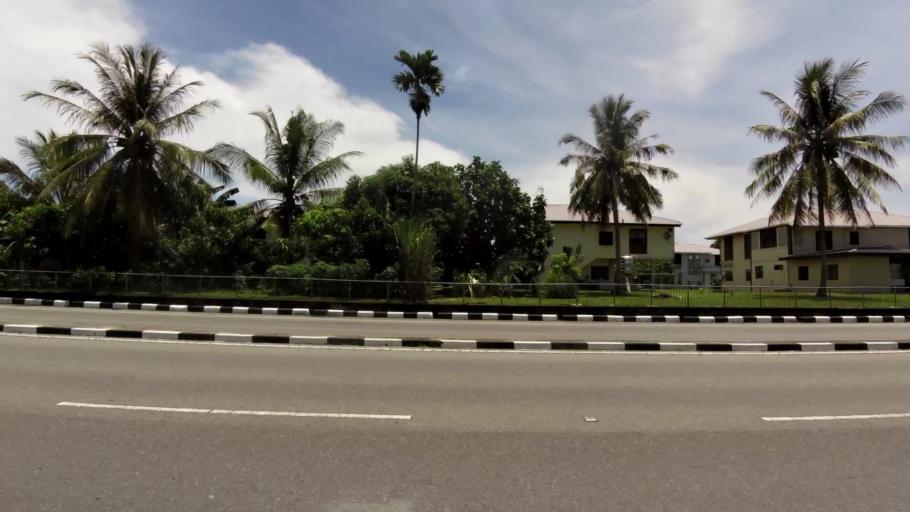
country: BN
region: Belait
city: Kuala Belait
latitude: 4.5825
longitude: 114.2373
